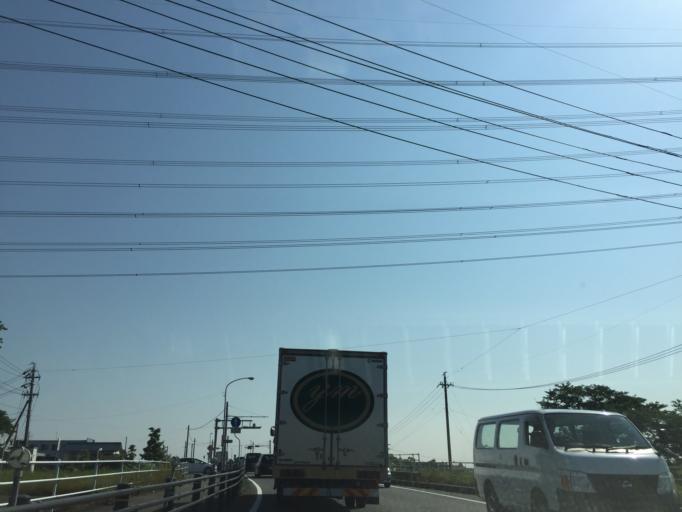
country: JP
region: Mie
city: Yokkaichi
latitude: 35.0426
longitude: 136.6743
